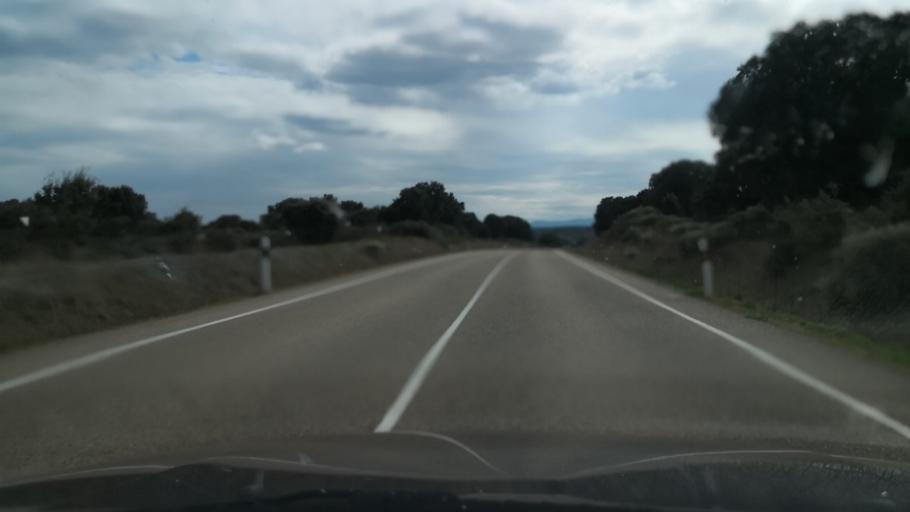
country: ES
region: Castille and Leon
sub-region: Provincia de Salamanca
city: Robleda
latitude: 40.4491
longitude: -6.5937
